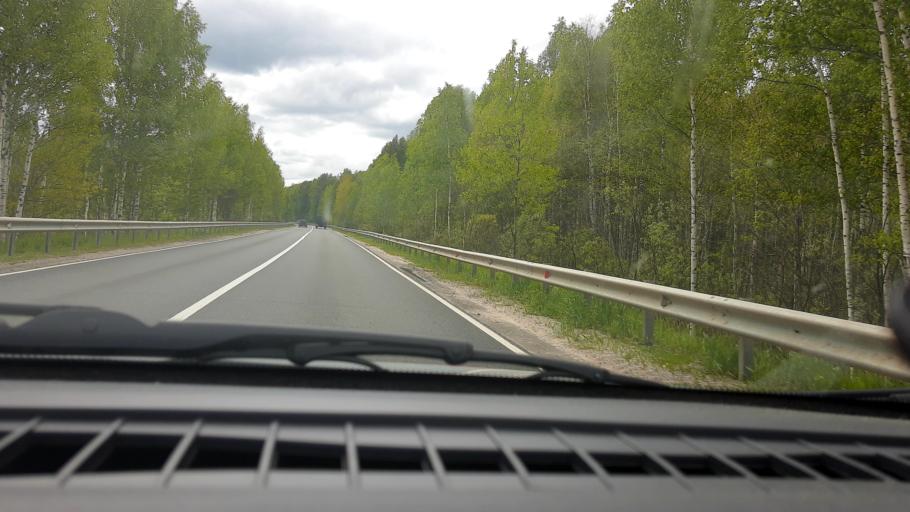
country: RU
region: Nizjnij Novgorod
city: Krasnyye Baki
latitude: 57.1346
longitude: 45.2157
